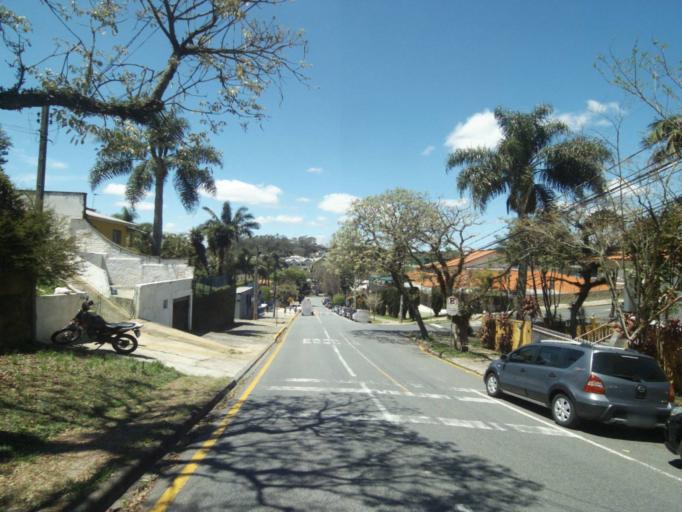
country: BR
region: Parana
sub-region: Curitiba
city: Curitiba
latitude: -25.3897
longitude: -49.2692
